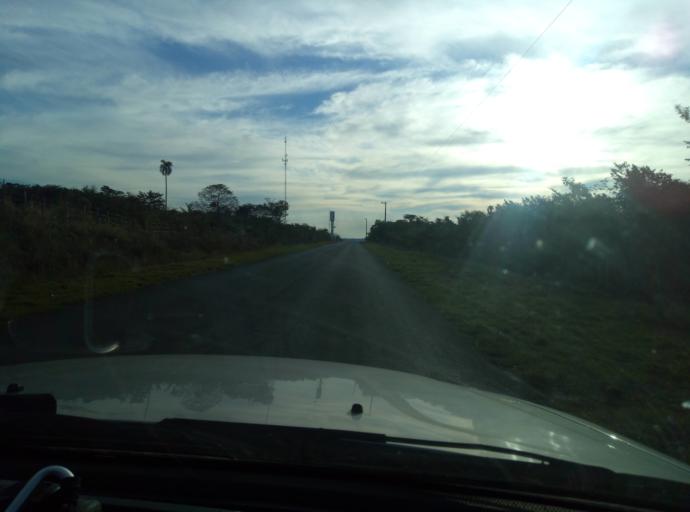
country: PY
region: Caaguazu
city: Carayao
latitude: -25.1534
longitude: -56.3229
